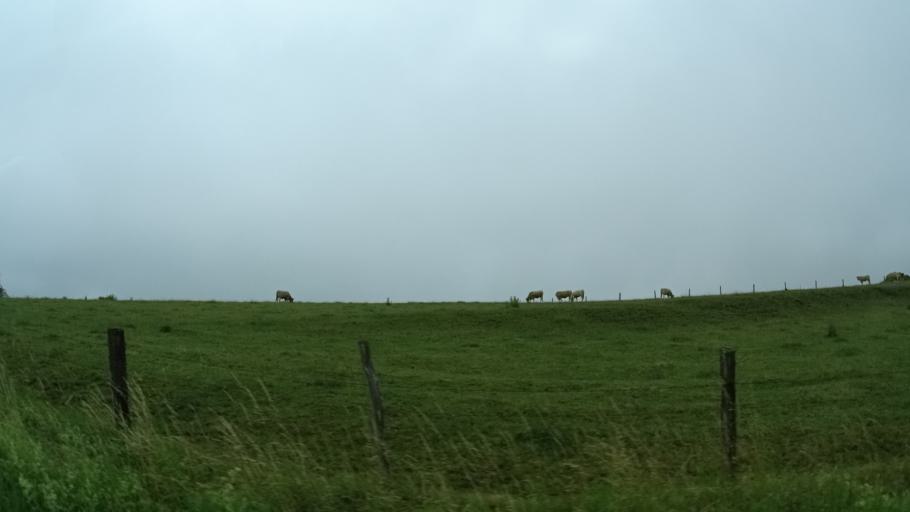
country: BE
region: Wallonia
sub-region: Province du Luxembourg
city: Leglise
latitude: 49.7830
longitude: 5.5561
